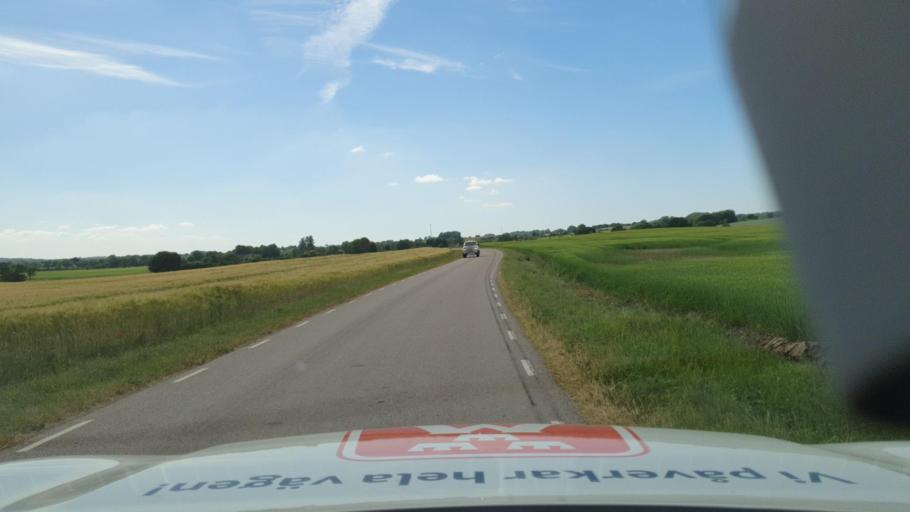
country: SE
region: Skane
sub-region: Sjobo Kommun
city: Sjoebo
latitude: 55.6380
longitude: 13.7965
